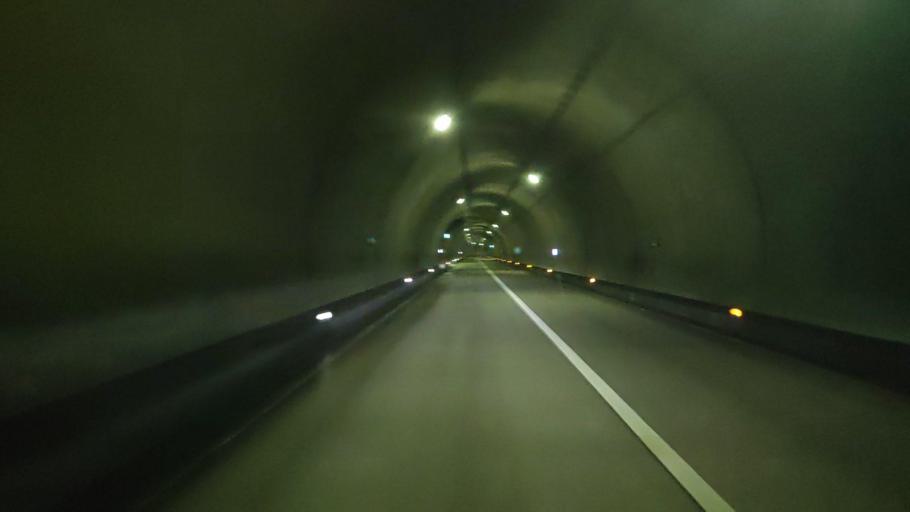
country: JP
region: Wakayama
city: Shingu
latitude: 33.8549
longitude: 135.8534
